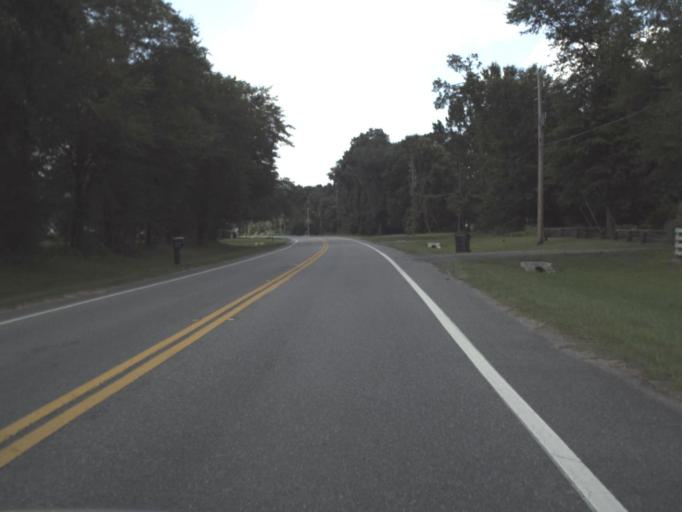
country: US
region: Florida
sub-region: Baker County
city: Macclenny
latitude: 30.3387
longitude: -82.1252
